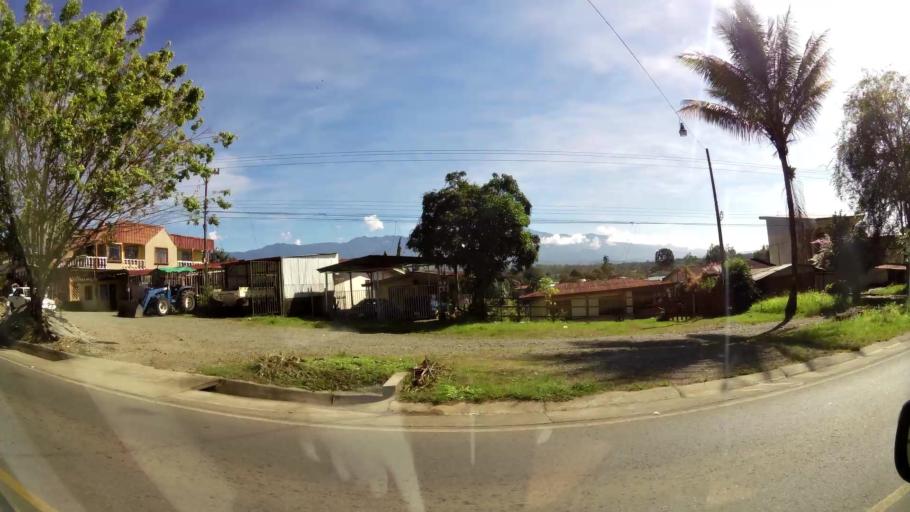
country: CR
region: San Jose
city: San Isidro
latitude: 9.3848
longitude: -83.7068
